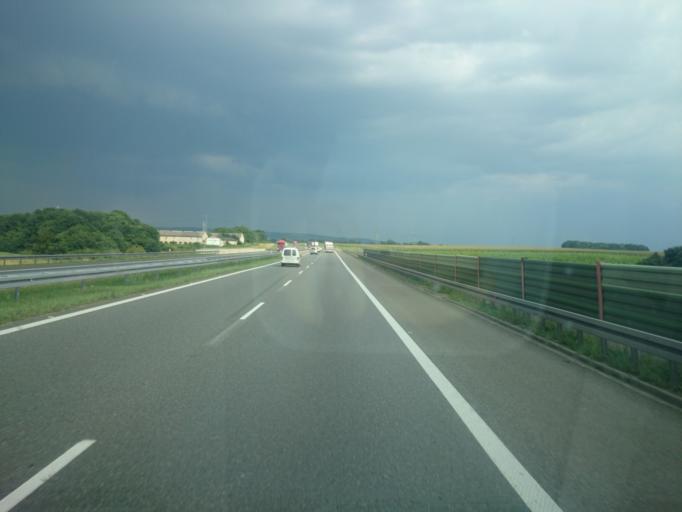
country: PL
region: Opole Voivodeship
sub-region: Powiat krapkowicki
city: Gogolin
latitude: 50.4799
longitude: 18.0618
